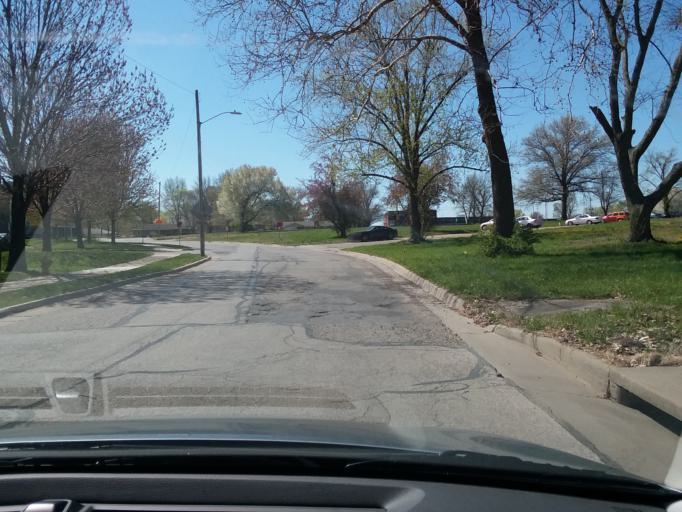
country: US
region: Kansas
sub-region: Douglas County
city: Lawrence
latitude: 38.9478
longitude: -95.2592
